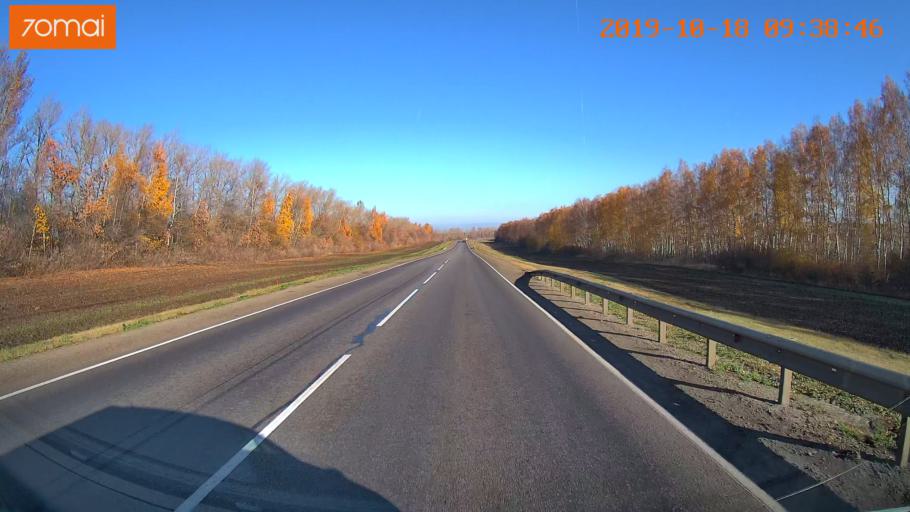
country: RU
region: Tula
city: Yefremov
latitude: 53.2429
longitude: 38.1358
